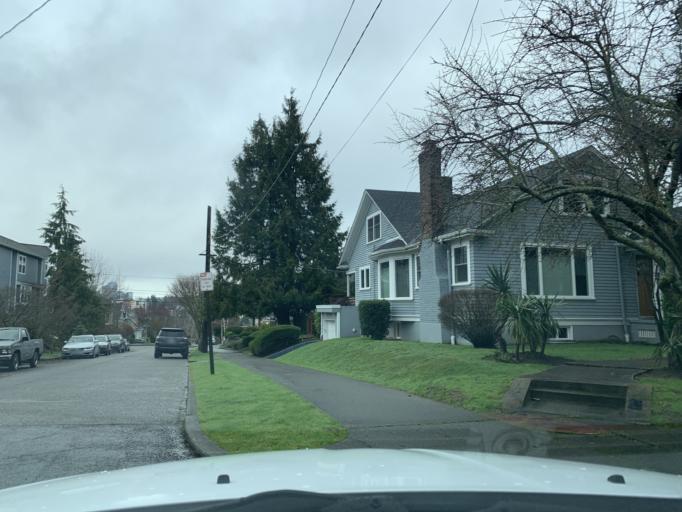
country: US
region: Washington
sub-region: King County
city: Seattle
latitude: 47.6141
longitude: -122.2904
